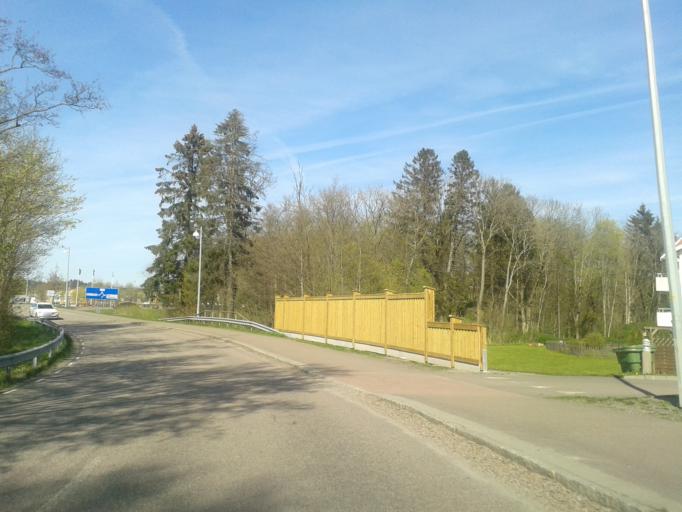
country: SE
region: Vaestra Goetaland
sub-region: Ale Kommun
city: Nodinge-Nol
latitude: 57.8907
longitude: 12.0454
